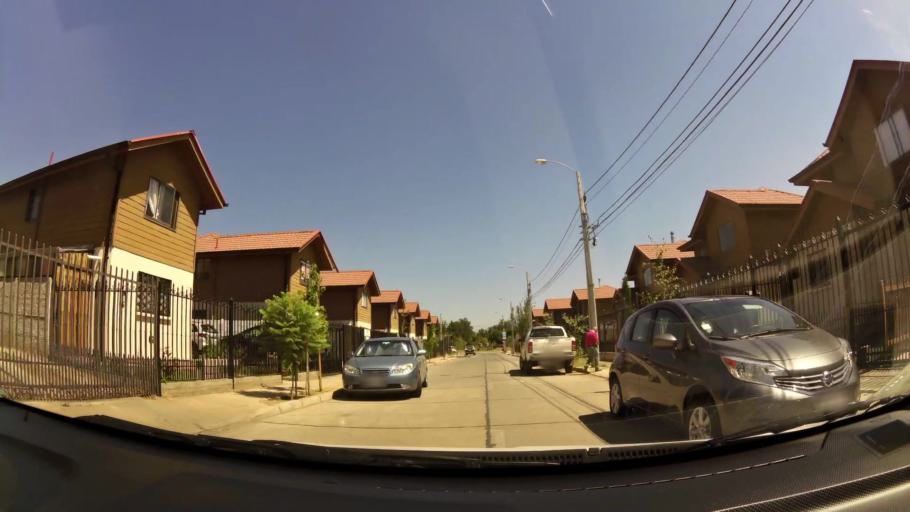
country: CL
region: Maule
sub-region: Provincia de Talca
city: Talca
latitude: -35.4307
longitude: -71.6060
